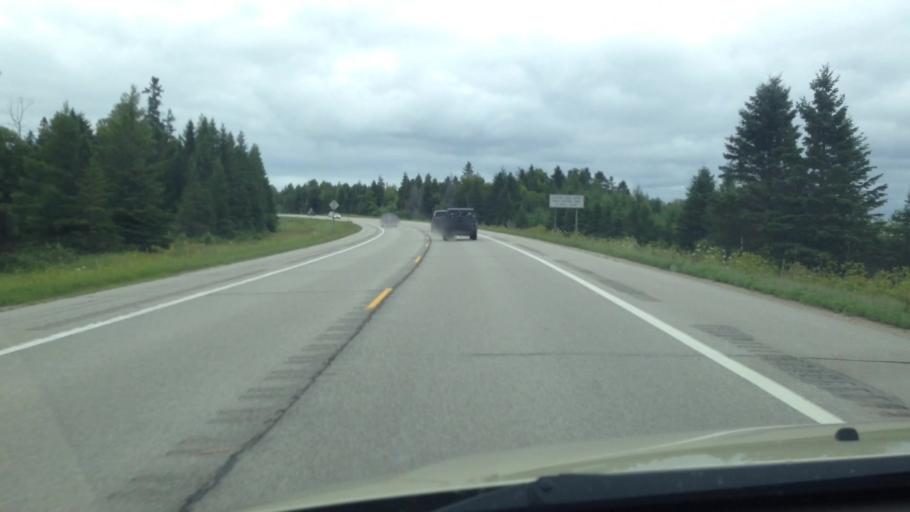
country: US
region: Michigan
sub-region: Luce County
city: Newberry
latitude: 46.0944
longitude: -85.4712
